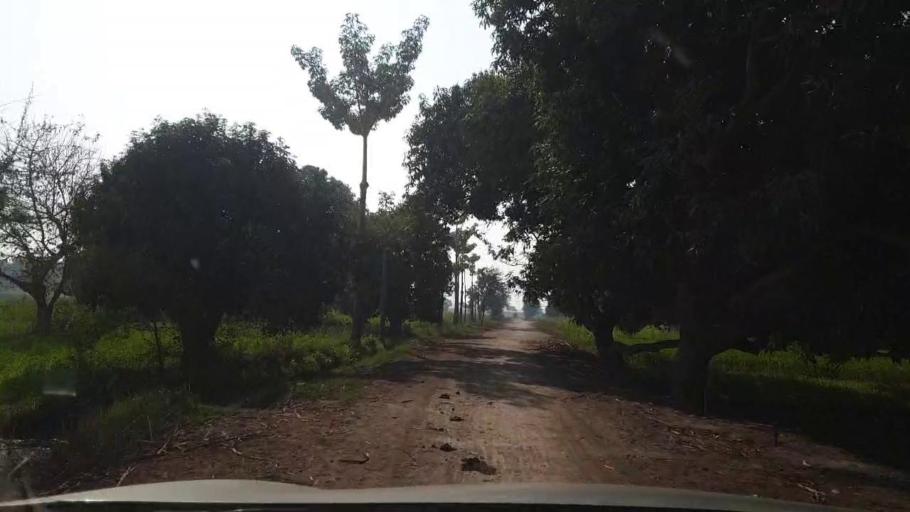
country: PK
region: Sindh
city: Tando Allahyar
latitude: 25.4692
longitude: 68.6330
